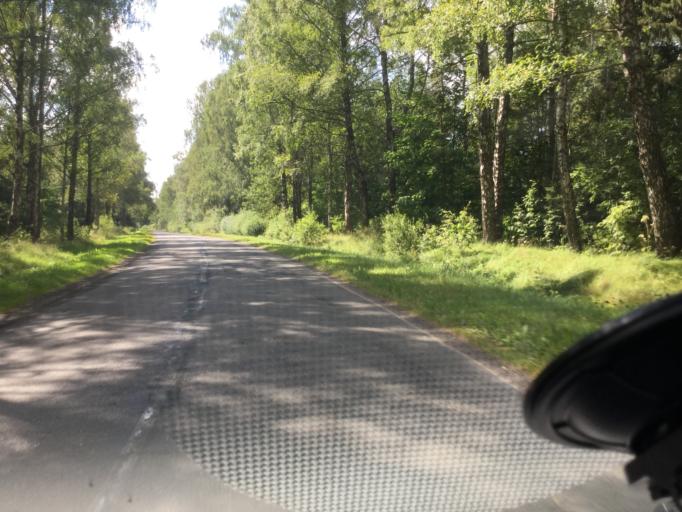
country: BY
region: Vitebsk
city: Chashniki
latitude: 55.2994
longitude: 29.3788
